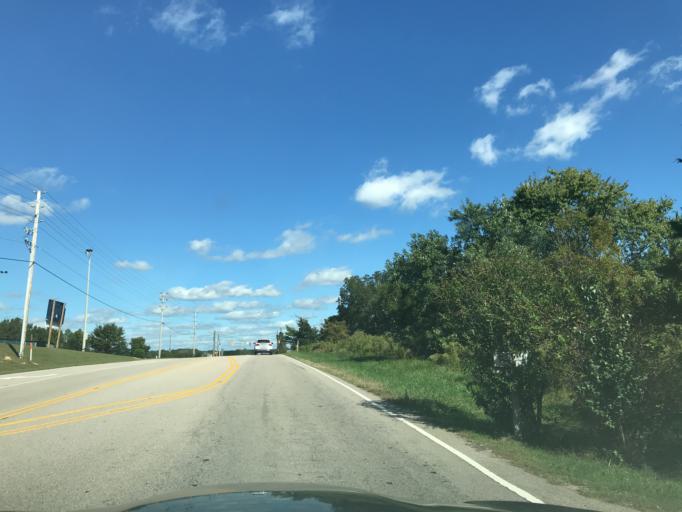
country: US
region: North Carolina
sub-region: Wake County
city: Wake Forest
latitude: 35.9414
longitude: -78.5073
